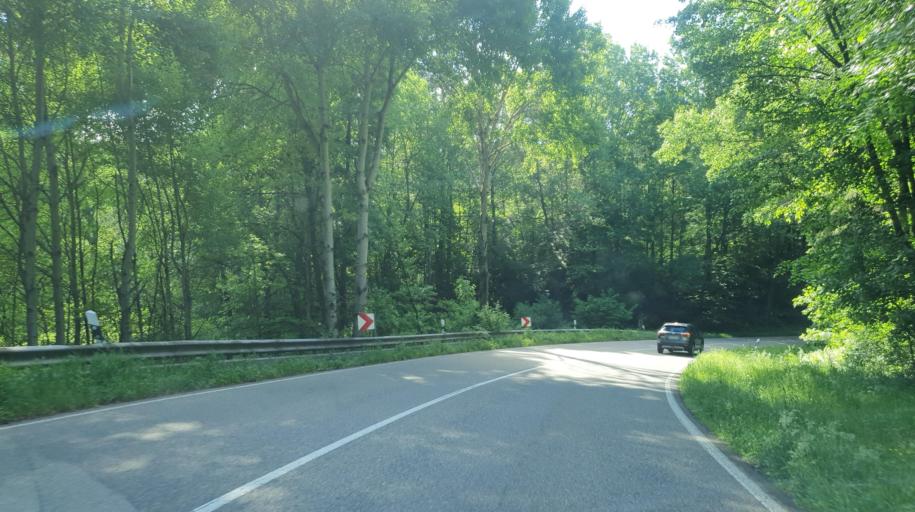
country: DE
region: Rheinland-Pfalz
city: Wernersberg
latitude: 49.1816
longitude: 7.9523
